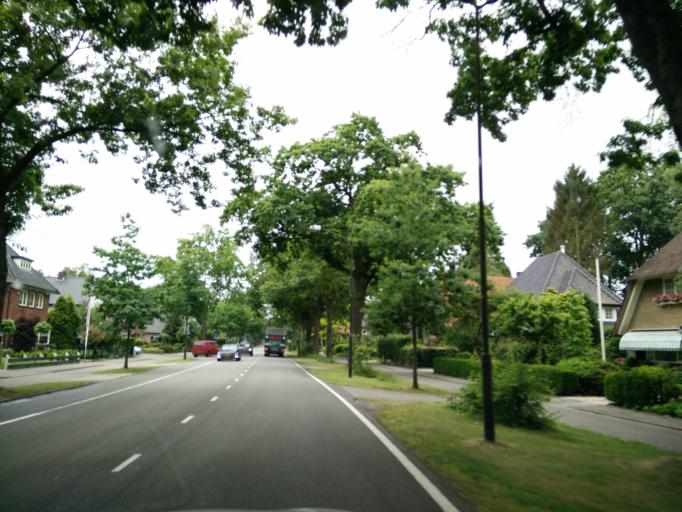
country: NL
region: Gelderland
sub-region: Gemeente Apeldoorn
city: Apeldoorn
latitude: 52.2151
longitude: 5.9328
